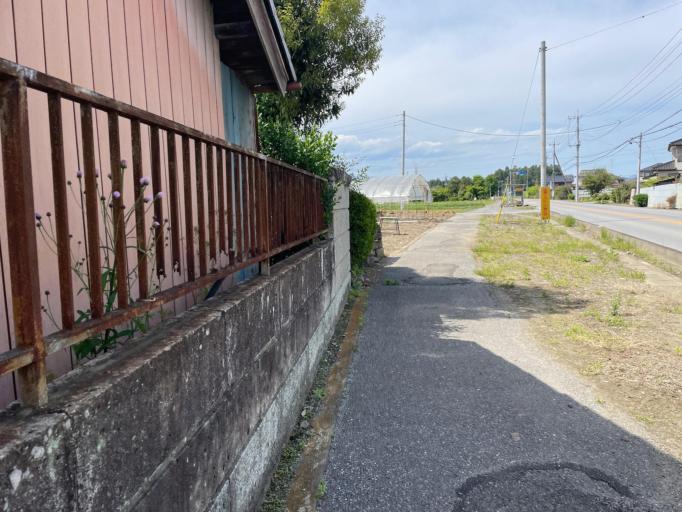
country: JP
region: Tochigi
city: Mibu
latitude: 36.4772
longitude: 139.7644
